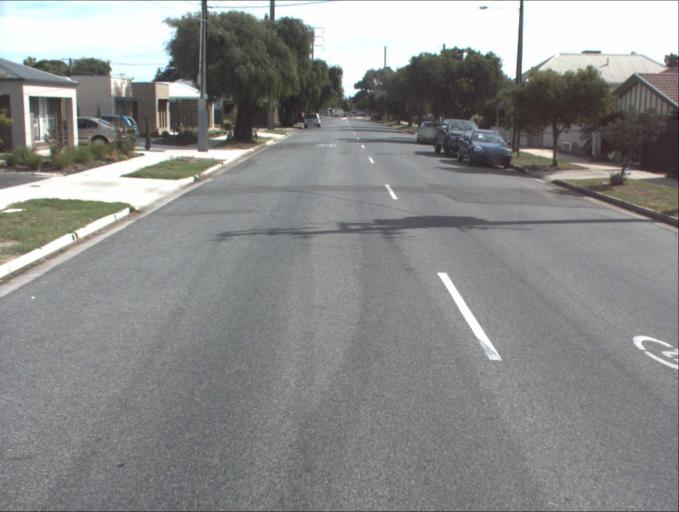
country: AU
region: South Australia
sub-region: Port Adelaide Enfield
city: Birkenhead
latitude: -34.8357
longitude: 138.4930
